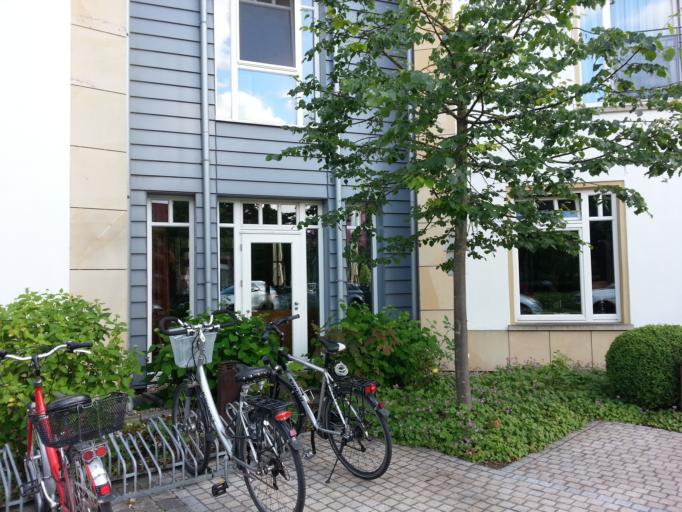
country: DE
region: North Rhine-Westphalia
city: Rietberg
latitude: 51.8110
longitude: 8.4278
